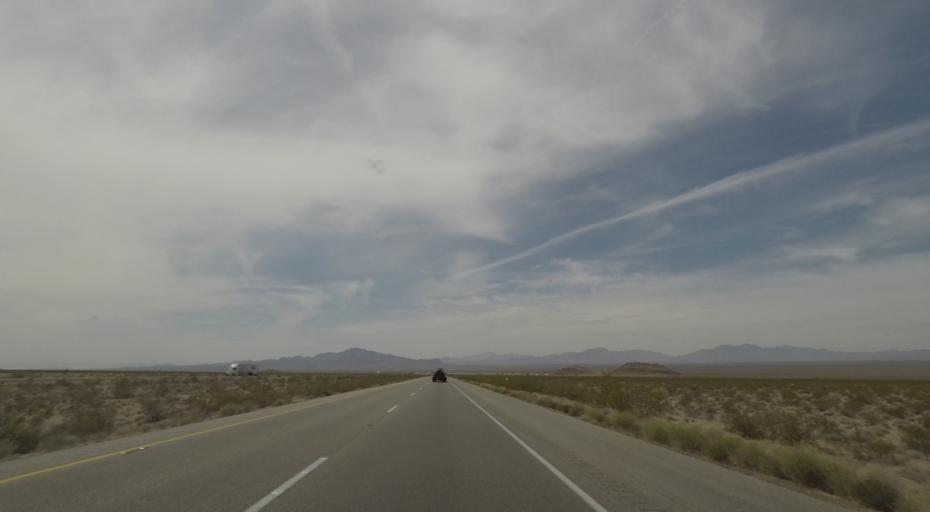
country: US
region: California
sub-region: San Bernardino County
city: Needles
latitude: 34.8180
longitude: -115.1469
